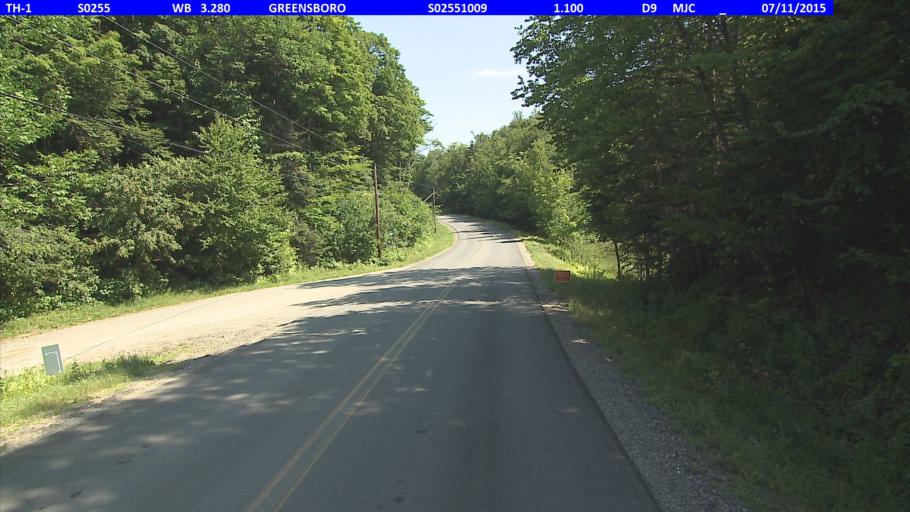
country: US
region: Vermont
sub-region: Caledonia County
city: Hardwick
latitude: 44.6256
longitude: -72.3293
